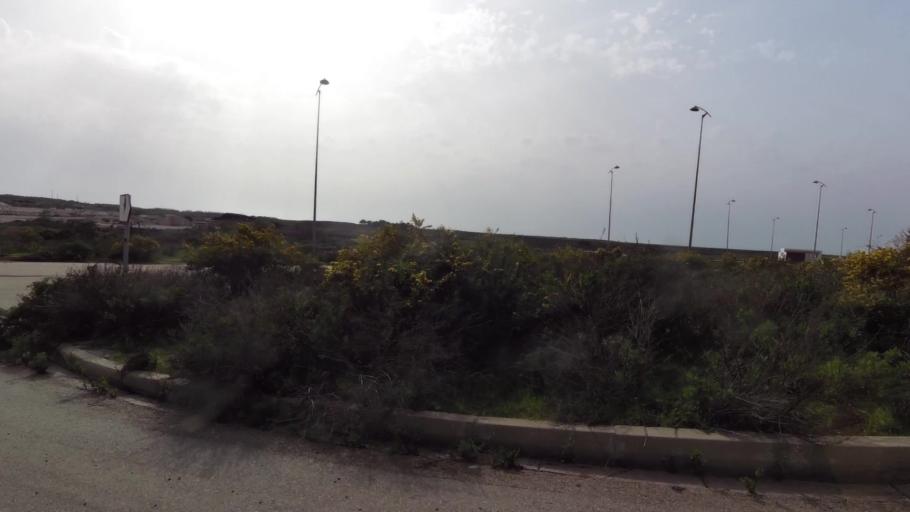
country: MA
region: Tanger-Tetouan
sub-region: Tanger-Assilah
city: Boukhalef
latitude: 35.6931
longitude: -5.9403
